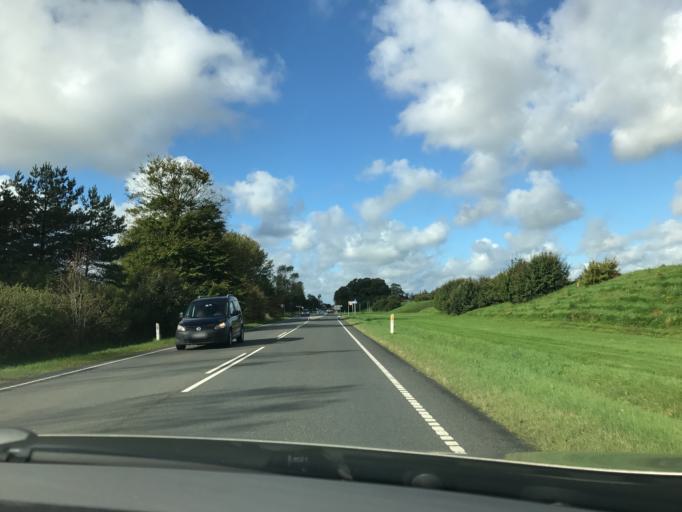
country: DK
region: South Denmark
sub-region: Billund Kommune
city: Billund
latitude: 55.7239
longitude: 9.1406
